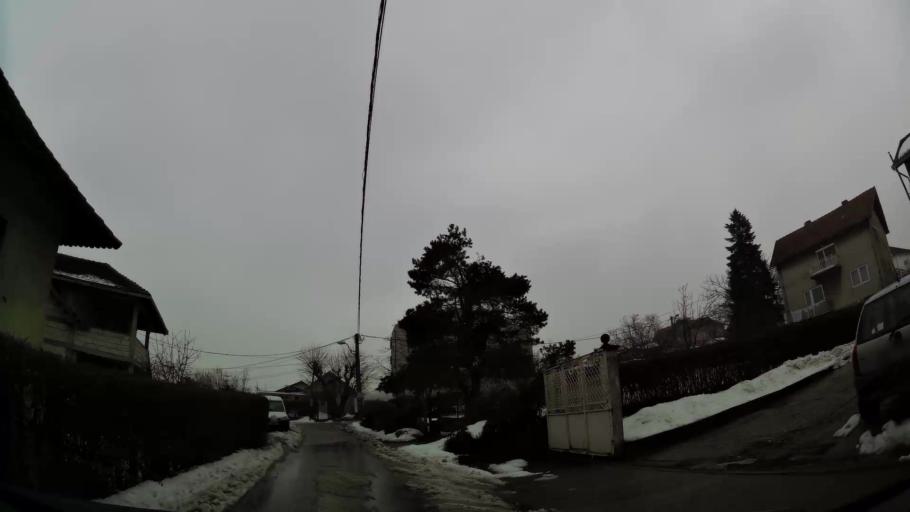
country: RS
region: Central Serbia
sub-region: Belgrade
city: Zvezdara
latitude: 44.7637
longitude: 20.5194
